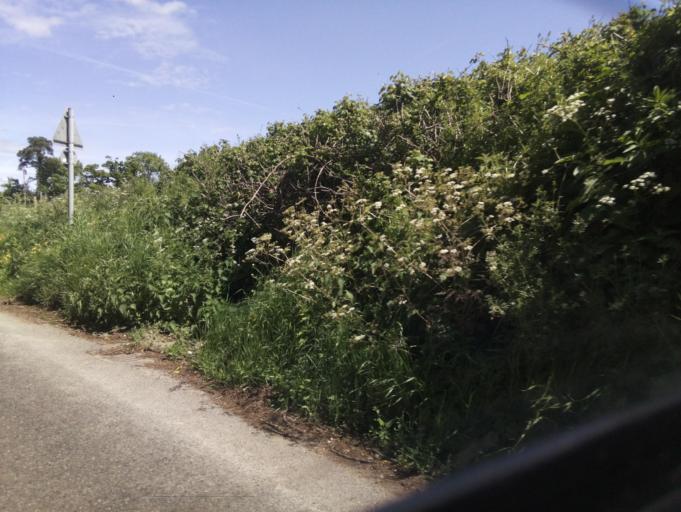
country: GB
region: England
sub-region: Devon
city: Honiton
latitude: 50.8125
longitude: -3.2356
